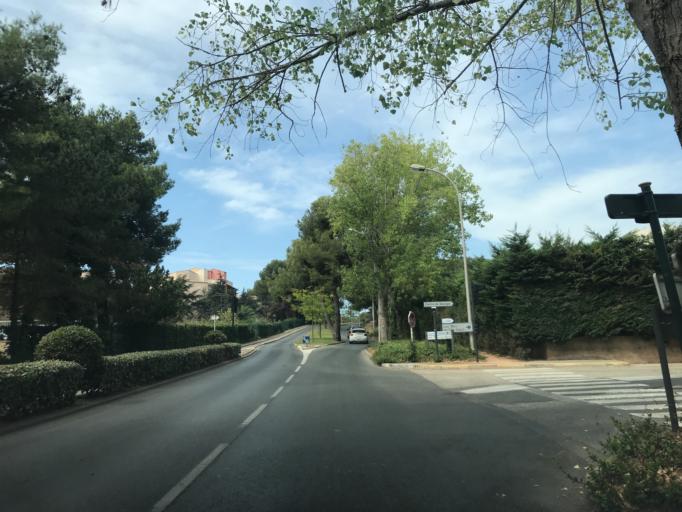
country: FR
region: Provence-Alpes-Cote d'Azur
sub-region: Departement du Var
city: Sanary-sur-Mer
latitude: 43.0999
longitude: 5.8151
